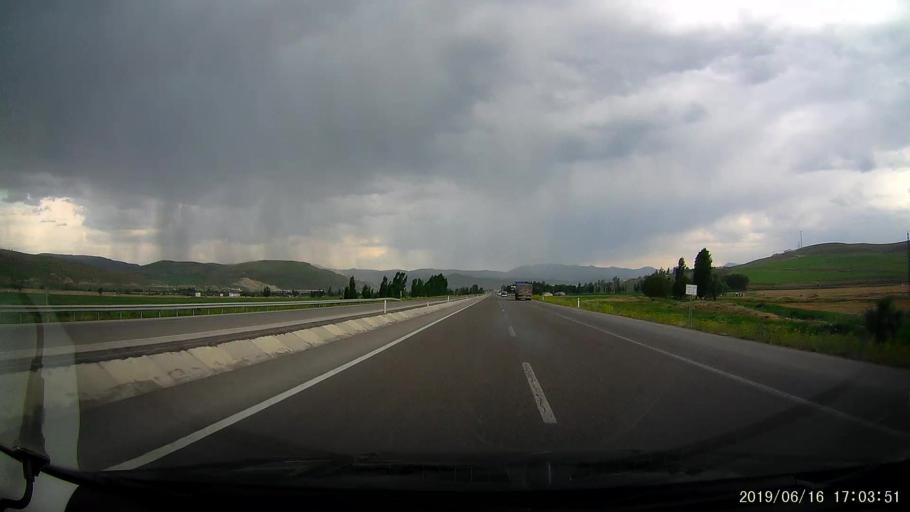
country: TR
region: Erzurum
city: Askale
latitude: 39.9322
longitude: 40.7220
